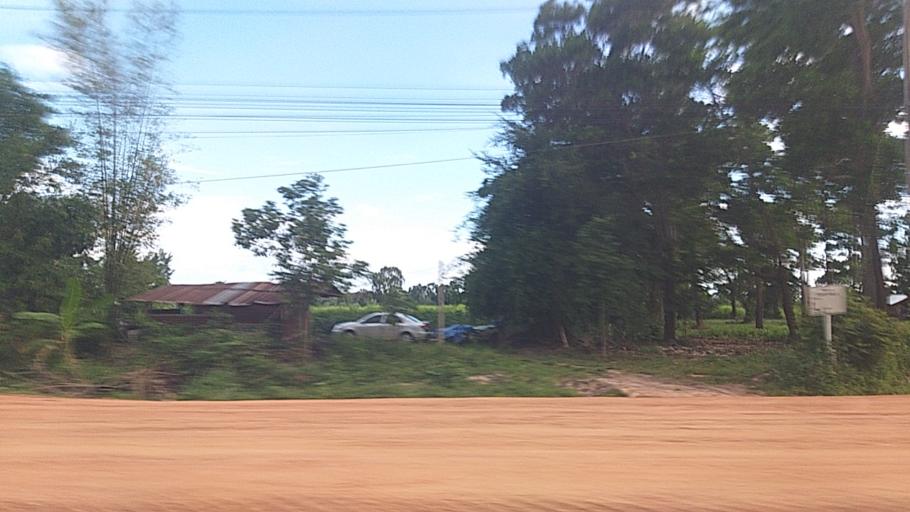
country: TH
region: Surin
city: Kap Choeng
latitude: 14.4626
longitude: 103.6507
